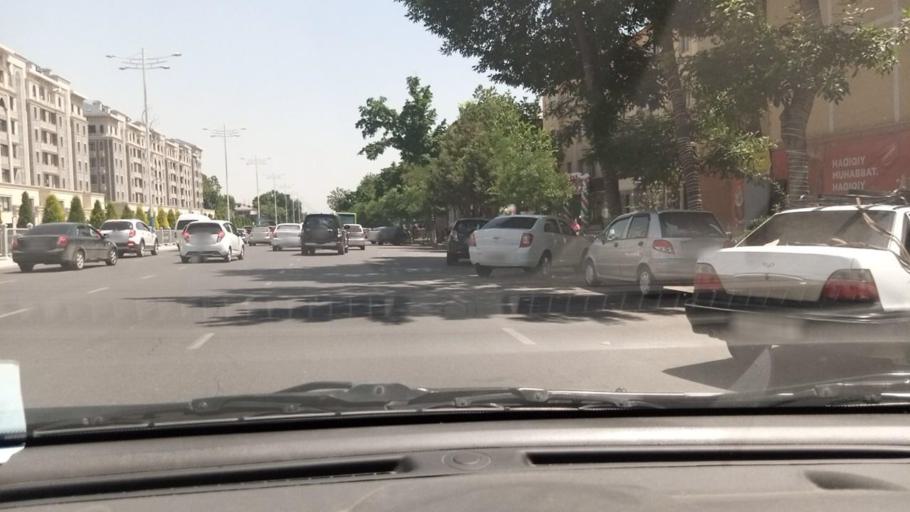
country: UZ
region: Toshkent Shahri
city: Tashkent
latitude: 41.2899
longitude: 69.2265
